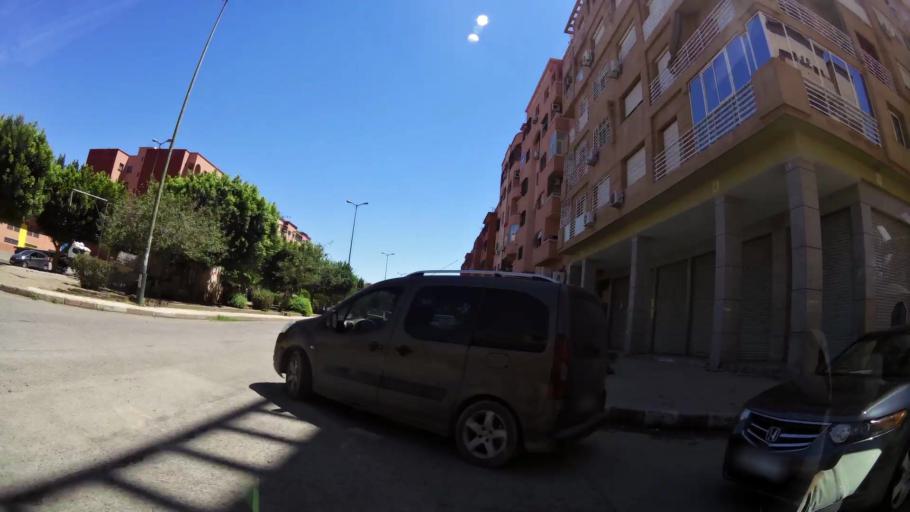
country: MA
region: Marrakech-Tensift-Al Haouz
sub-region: Marrakech
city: Marrakesh
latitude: 31.6340
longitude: -8.0608
